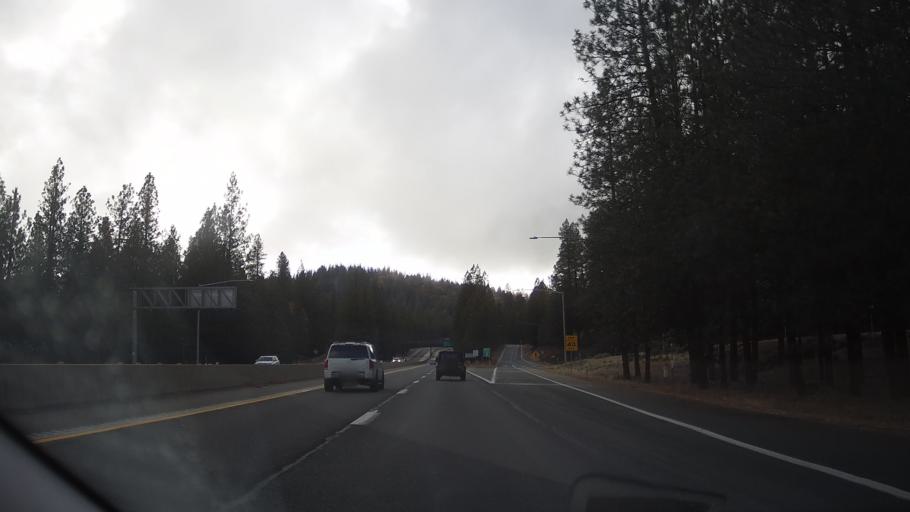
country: US
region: California
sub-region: Placer County
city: Colfax
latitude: 39.1783
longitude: -120.8544
